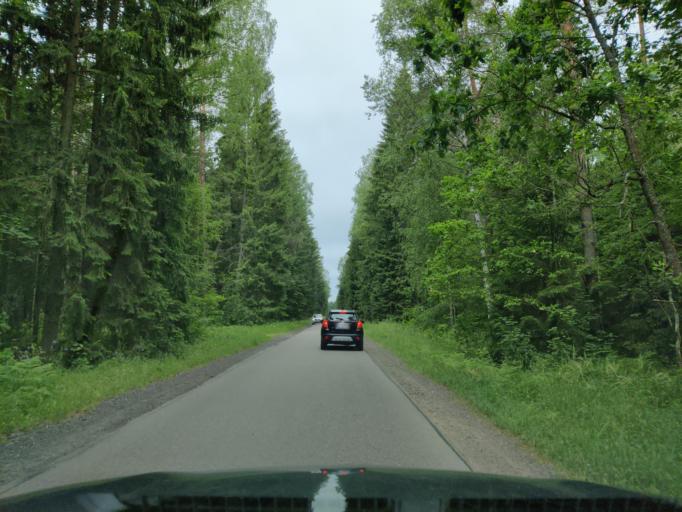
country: PL
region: Warmian-Masurian Voivodeship
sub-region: Powiat szczycienski
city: Rozogi
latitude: 53.5500
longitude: 21.4568
